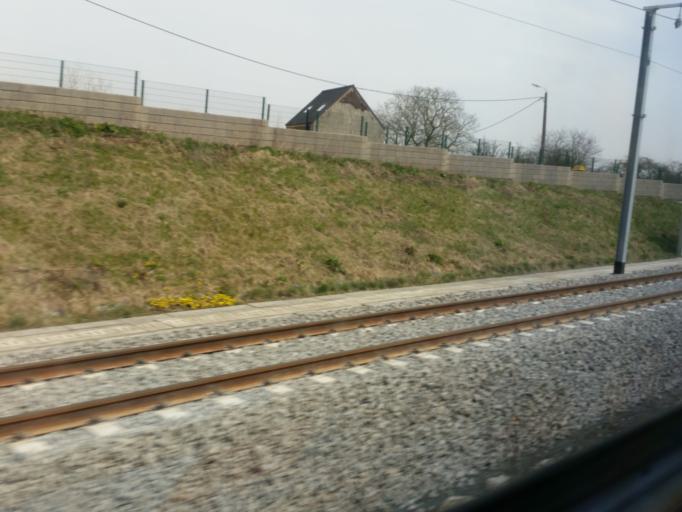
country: BE
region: Flanders
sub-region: Provincie Vlaams-Brabant
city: Dilbeek
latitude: 50.8238
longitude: 4.2439
